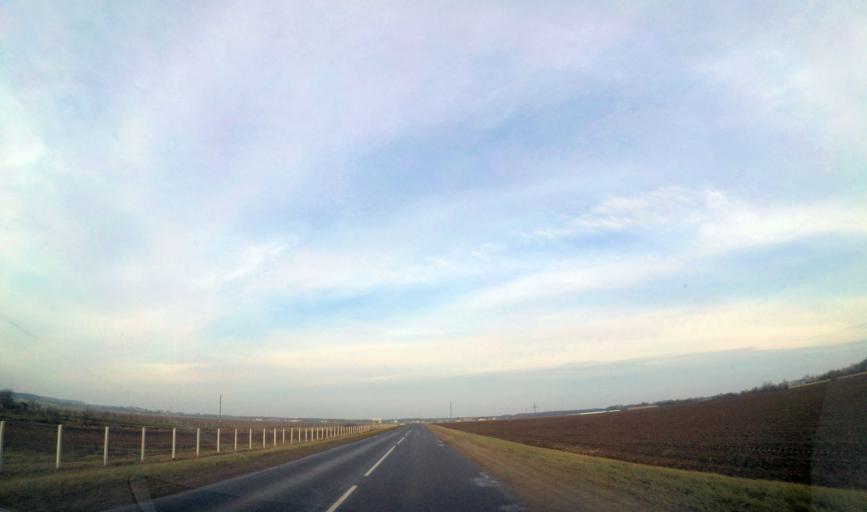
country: BY
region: Grodnenskaya
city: Hrodna
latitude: 53.7354
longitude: 23.9290
